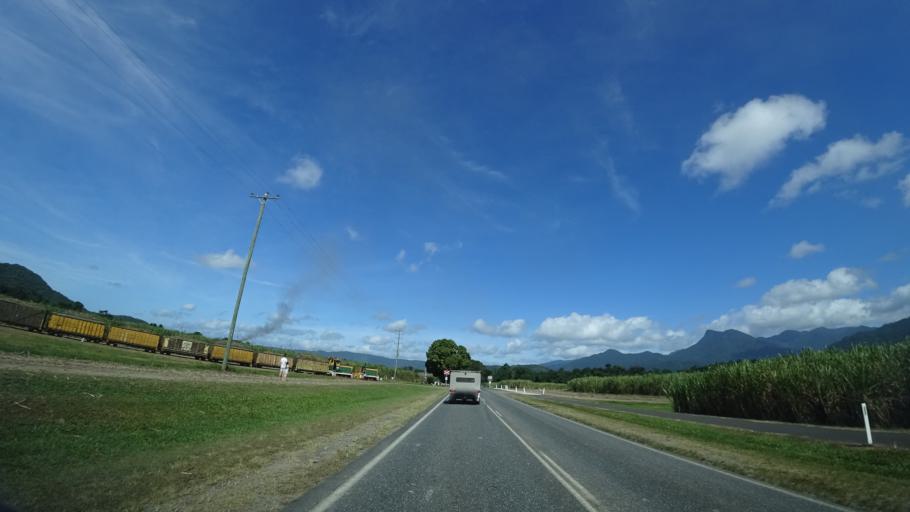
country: AU
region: Queensland
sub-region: Cairns
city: Port Douglas
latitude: -16.4462
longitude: 145.3725
